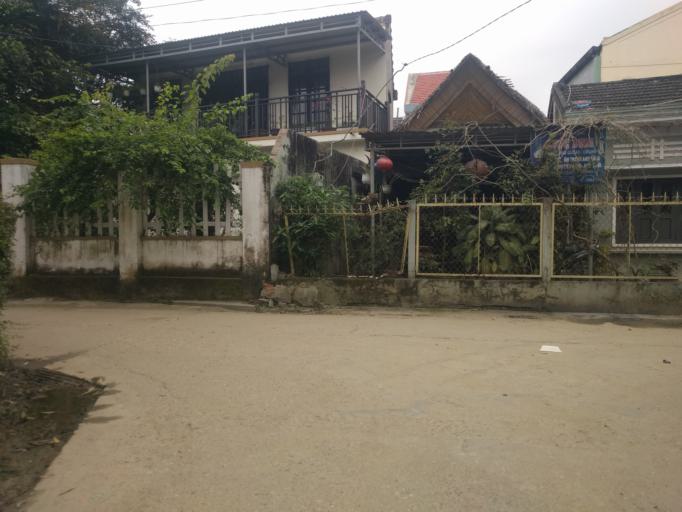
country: VN
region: Quang Nam
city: Hoi An
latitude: 15.8737
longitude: 108.3307
